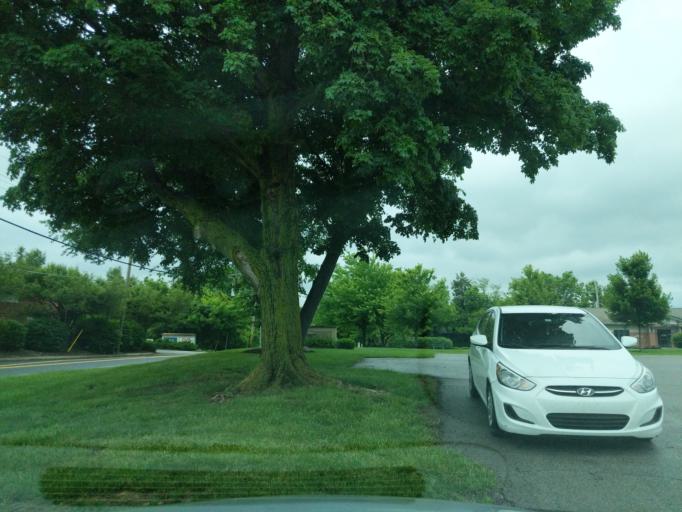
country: US
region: Indiana
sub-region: Hamilton County
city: Noblesville
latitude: 40.0476
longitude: -86.0239
